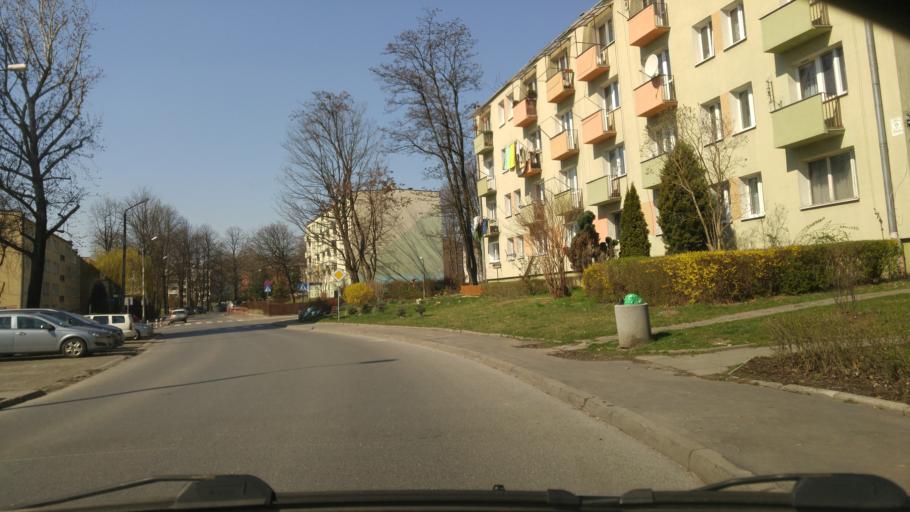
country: PL
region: Lesser Poland Voivodeship
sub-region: Powiat wielicki
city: Kokotow
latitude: 50.0963
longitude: 20.0630
